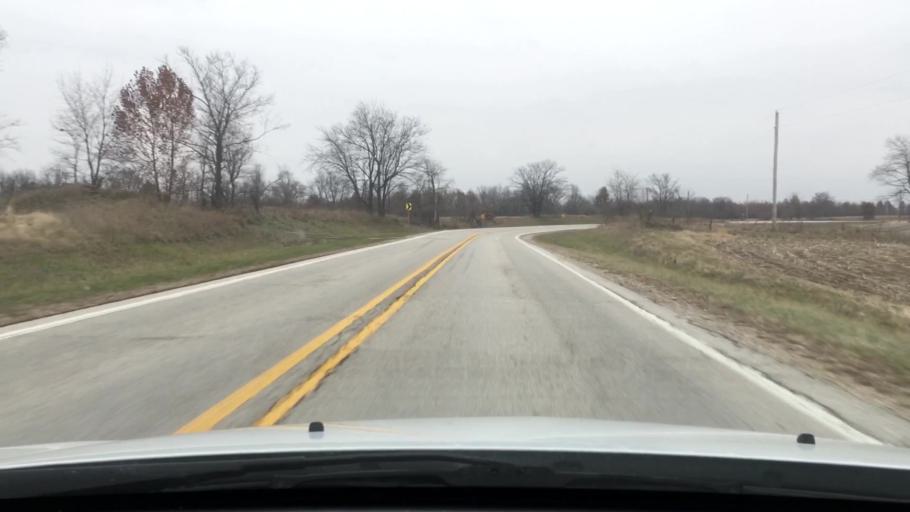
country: US
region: Illinois
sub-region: Pike County
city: Pittsfield
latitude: 39.5905
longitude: -90.8979
